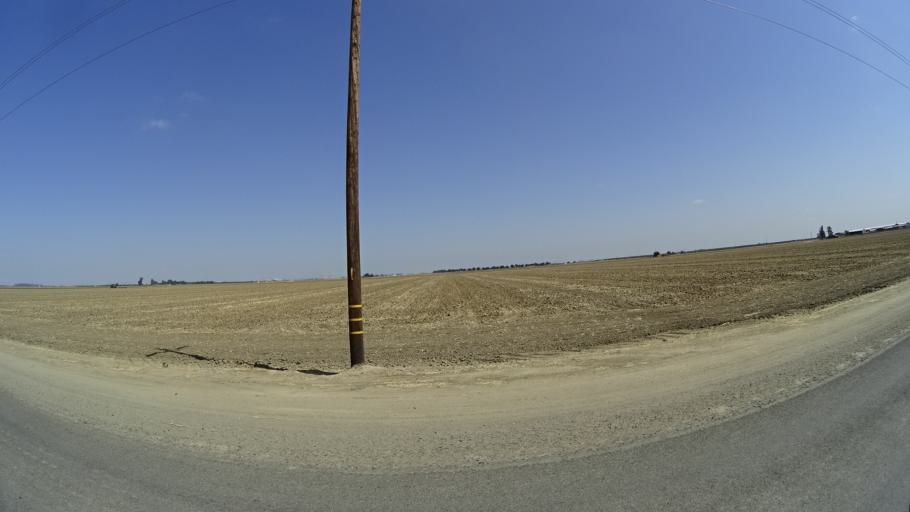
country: US
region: California
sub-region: Kings County
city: Home Garden
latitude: 36.2259
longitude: -119.6244
